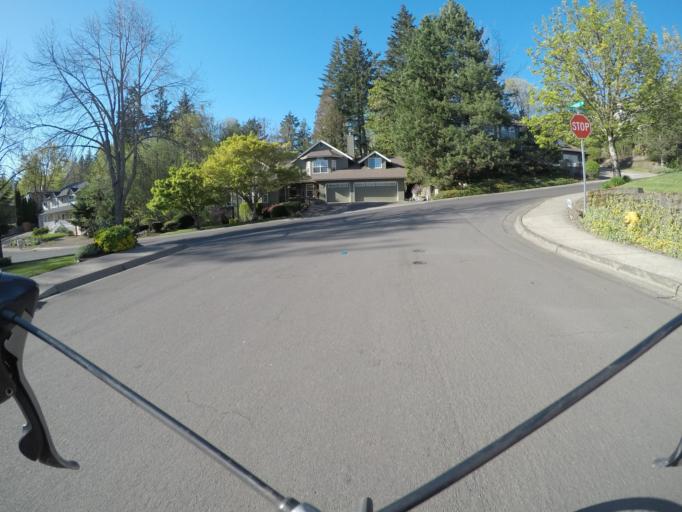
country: US
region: Oregon
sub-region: Washington County
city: King City
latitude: 45.4069
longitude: -122.8272
